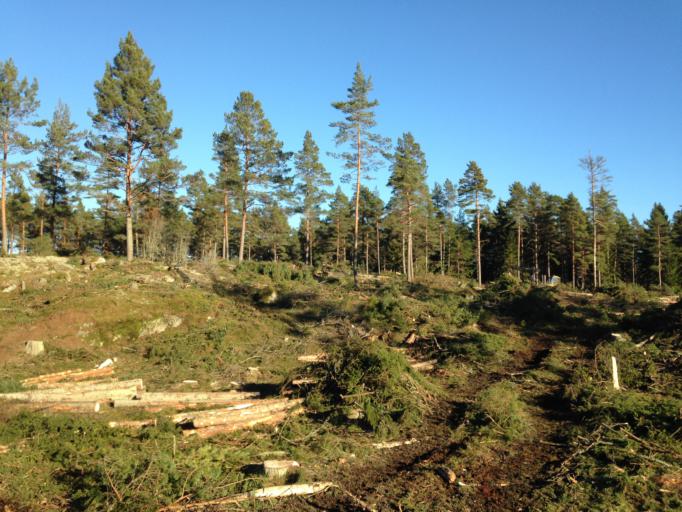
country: SE
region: Soedermanland
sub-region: Nykopings Kommun
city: Svalsta
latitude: 58.4877
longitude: 16.8758
